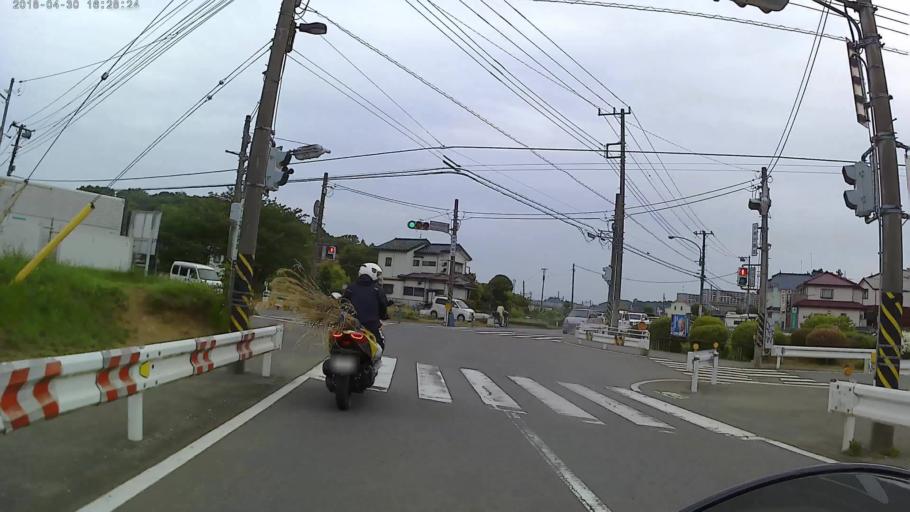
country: JP
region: Kanagawa
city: Zama
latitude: 35.4637
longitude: 139.4074
